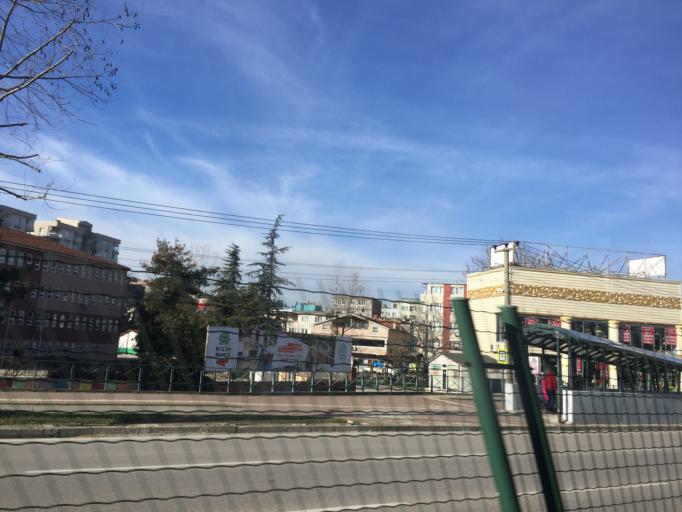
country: TR
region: Bursa
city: Yildirim
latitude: 40.2197
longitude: 28.9973
